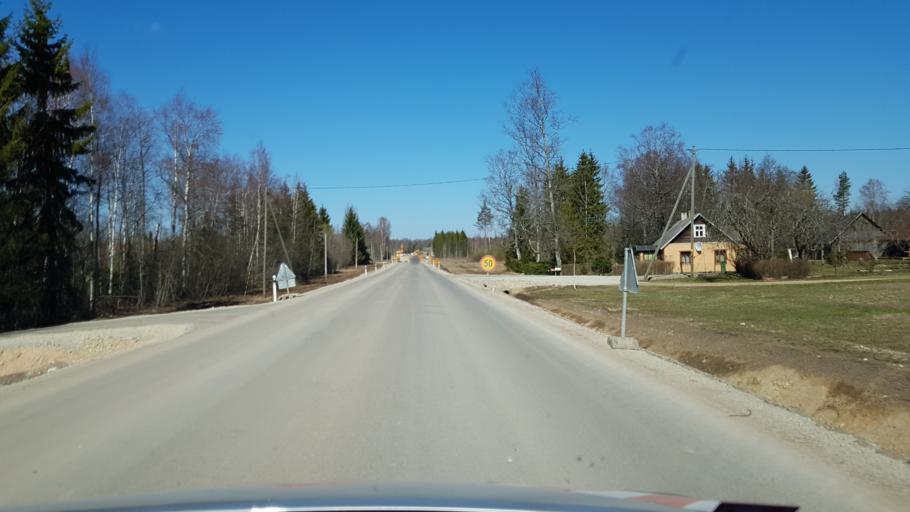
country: EE
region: Jogevamaa
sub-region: Mustvee linn
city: Mustvee
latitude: 59.0309
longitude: 26.6887
